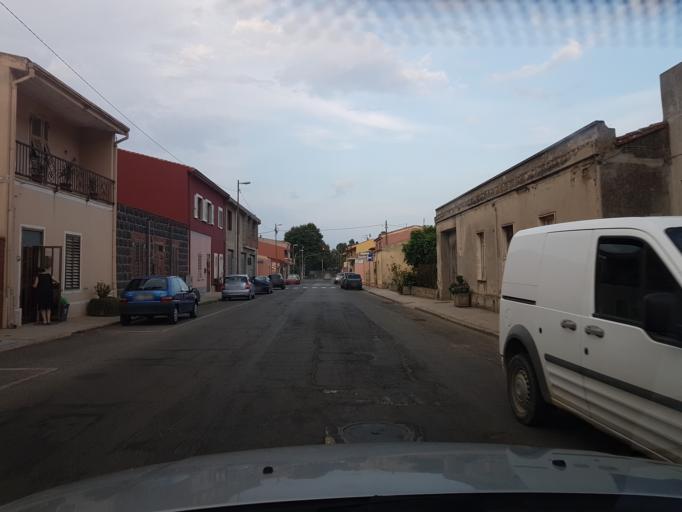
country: IT
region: Sardinia
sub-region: Provincia di Oristano
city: Cabras
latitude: 39.9295
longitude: 8.5368
